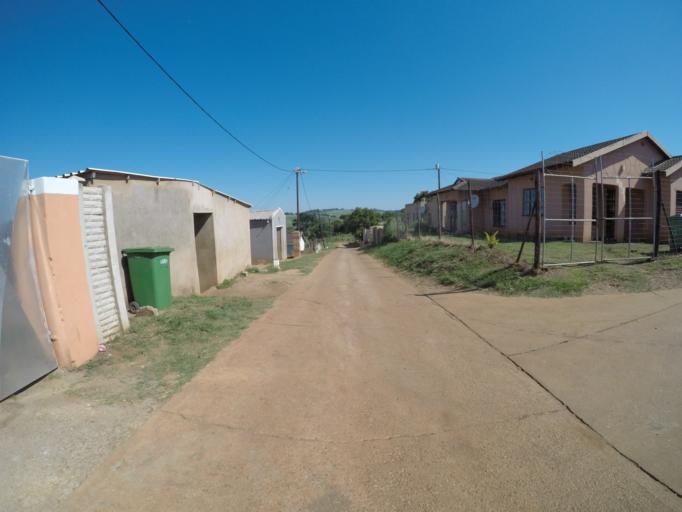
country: ZA
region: KwaZulu-Natal
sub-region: uThungulu District Municipality
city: Empangeni
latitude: -28.7771
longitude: 31.8790
